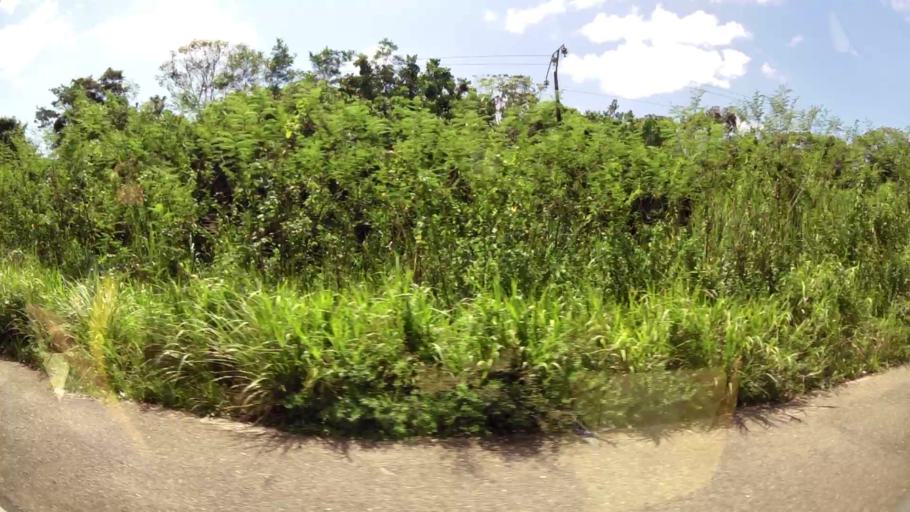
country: GF
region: Guyane
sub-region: Guyane
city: Matoury
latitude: 4.8622
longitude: -52.3334
